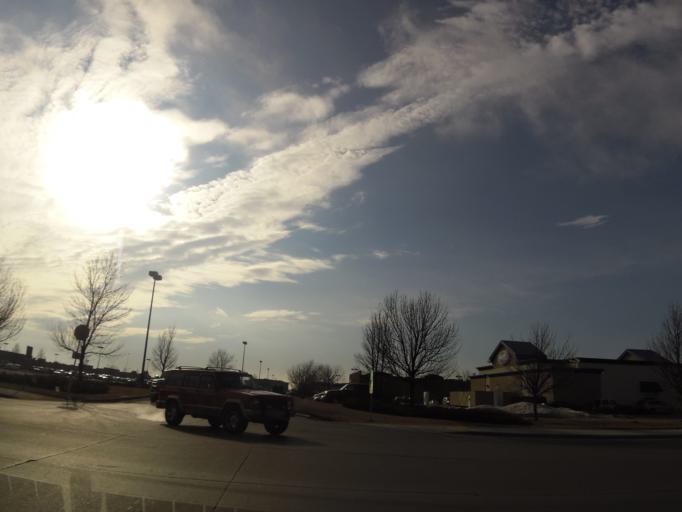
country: US
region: North Dakota
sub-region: Grand Forks County
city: Grand Forks
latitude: 47.8884
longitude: -97.0774
